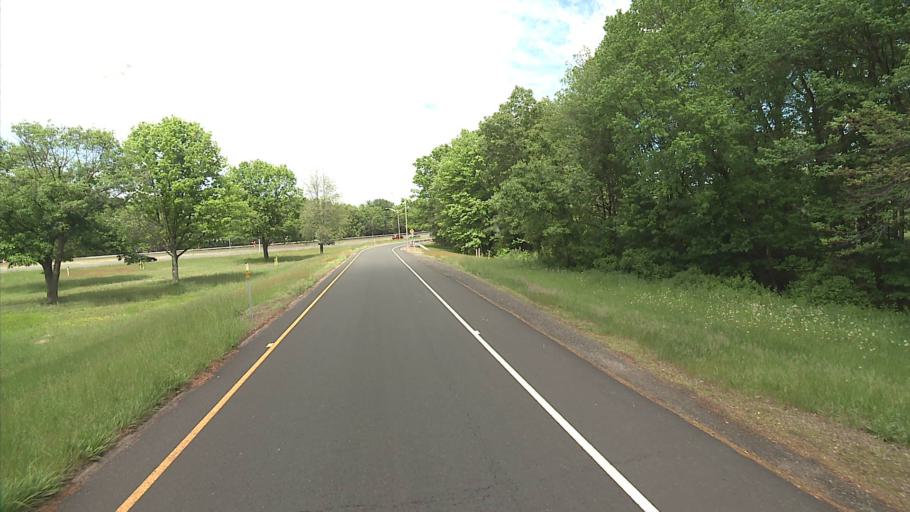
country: US
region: Connecticut
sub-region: New Haven County
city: North Haven
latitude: 41.3990
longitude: -72.8489
